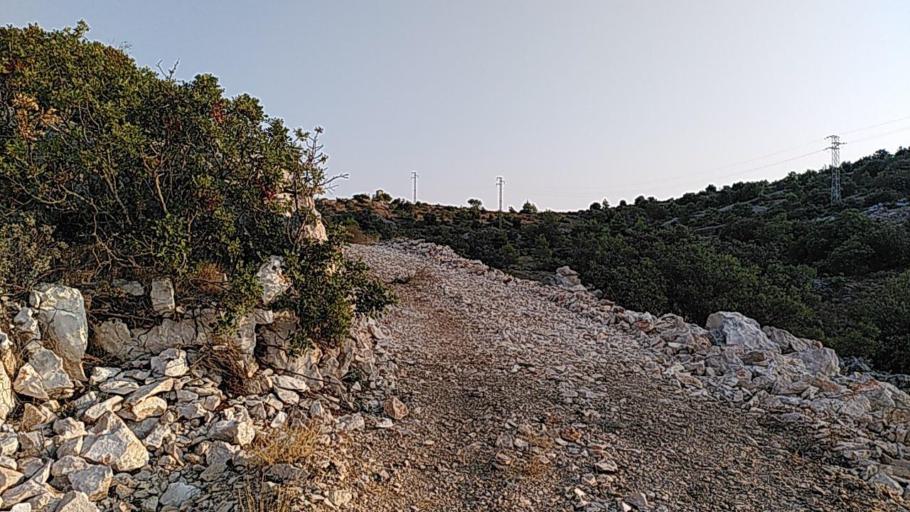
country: HR
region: Splitsko-Dalmatinska
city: Jelsa
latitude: 43.1334
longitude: 16.6805
